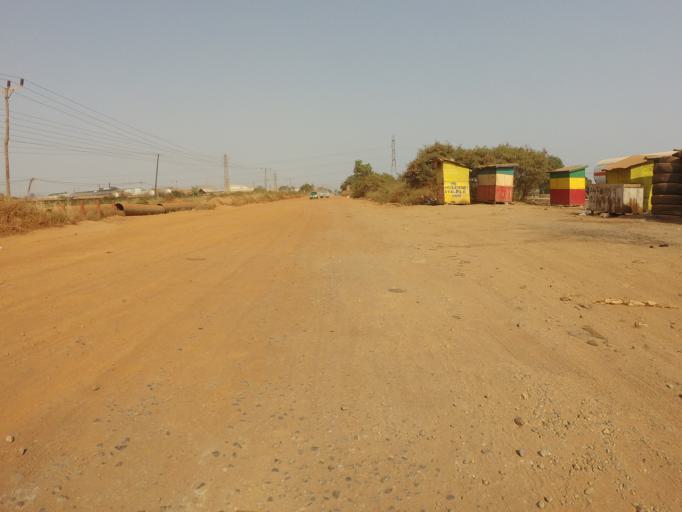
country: GH
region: Greater Accra
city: Tema
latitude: 5.6669
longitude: 0.0099
